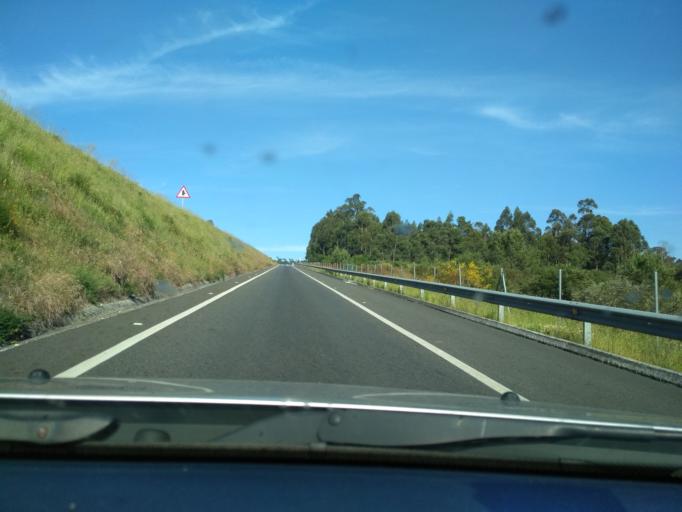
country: ES
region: Galicia
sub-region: Provincia da Coruna
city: Ames
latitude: 42.8607
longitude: -8.5994
